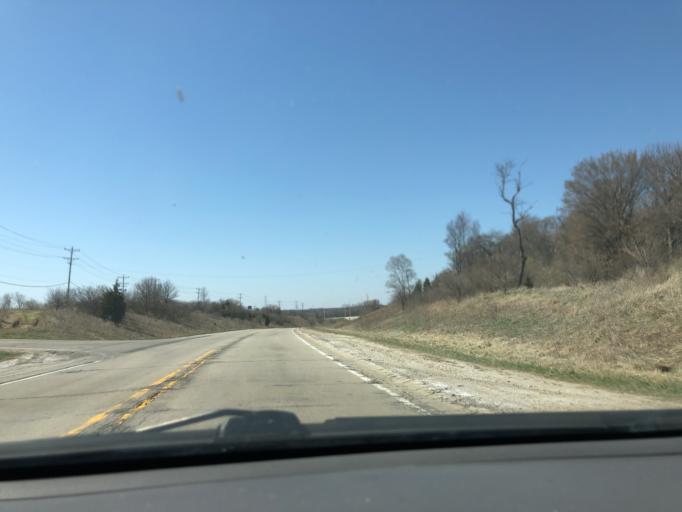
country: US
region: Illinois
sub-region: Kane County
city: Hampshire
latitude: 42.1387
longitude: -88.5038
